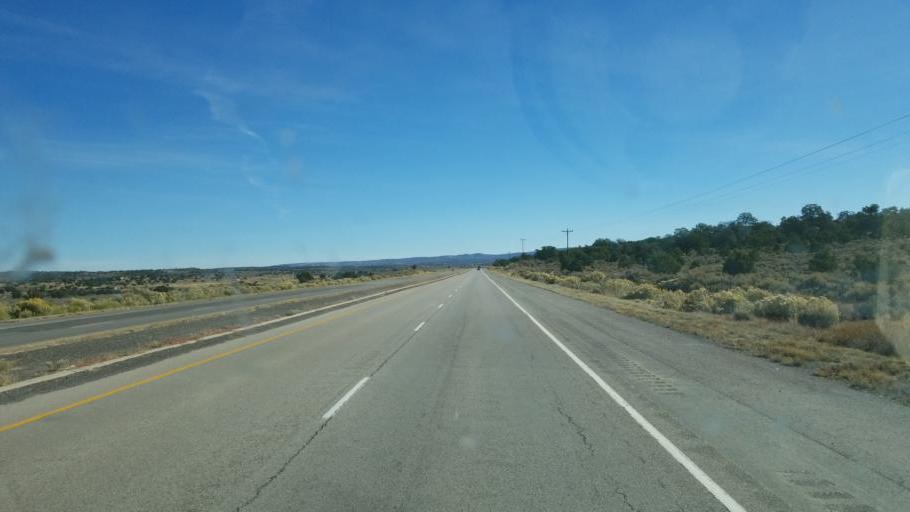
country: US
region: New Mexico
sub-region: McKinley County
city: Twin Lakes
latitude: 35.6358
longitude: -108.8592
